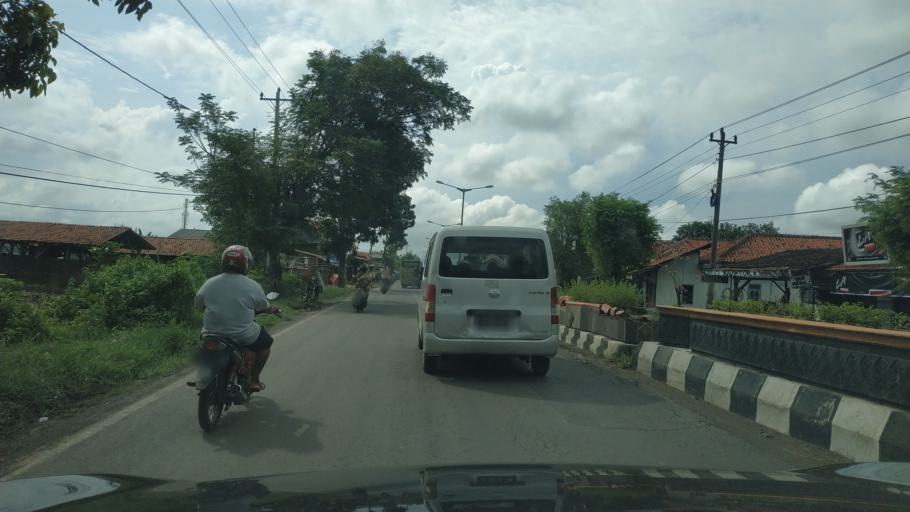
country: ID
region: Central Java
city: Pemalang
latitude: -6.9198
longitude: 109.3841
